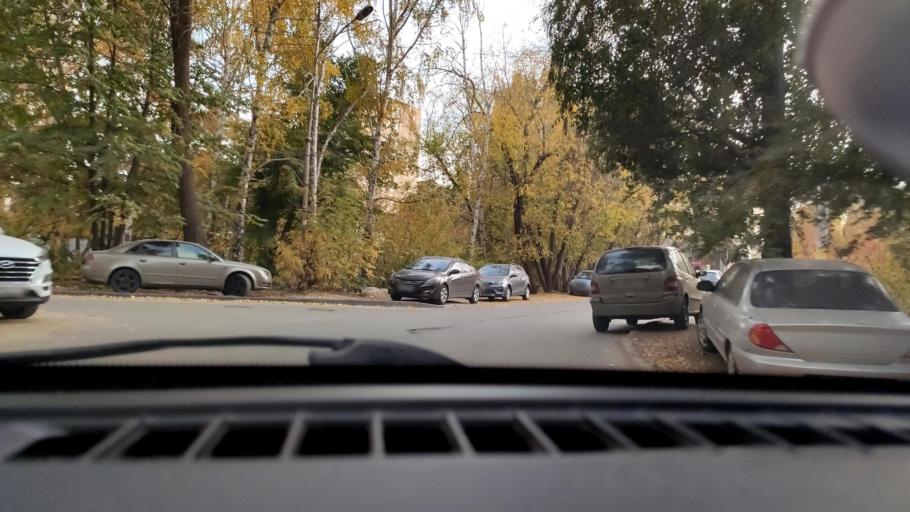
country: RU
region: Samara
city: Samara
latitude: 53.2176
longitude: 50.1601
